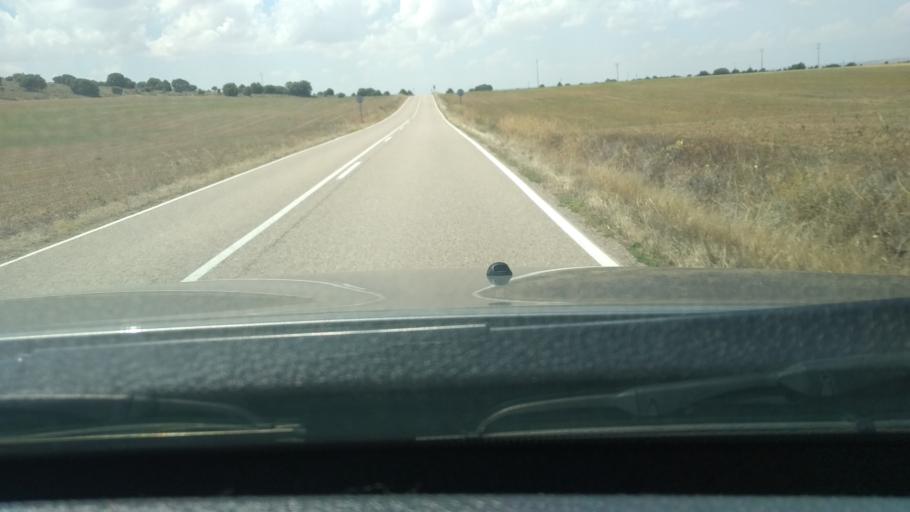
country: ES
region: Castille and Leon
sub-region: Provincia de Burgos
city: Avellanosa de Muno
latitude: 41.9765
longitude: -3.8032
